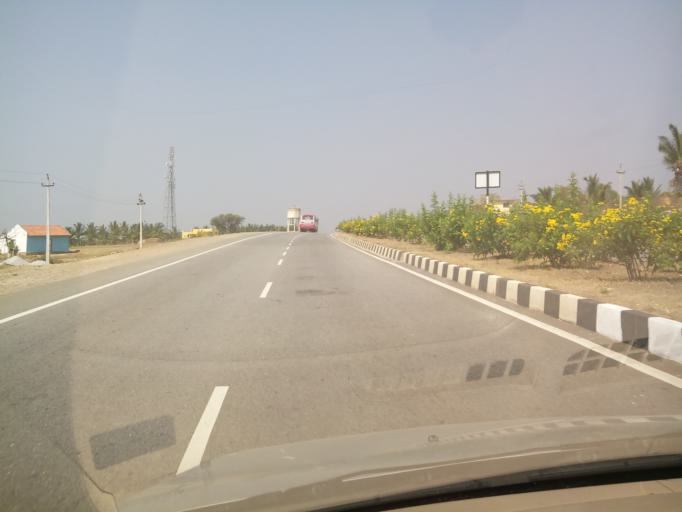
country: IN
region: Karnataka
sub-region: Hassan
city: Shravanabelagola
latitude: 12.9195
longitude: 76.4728
